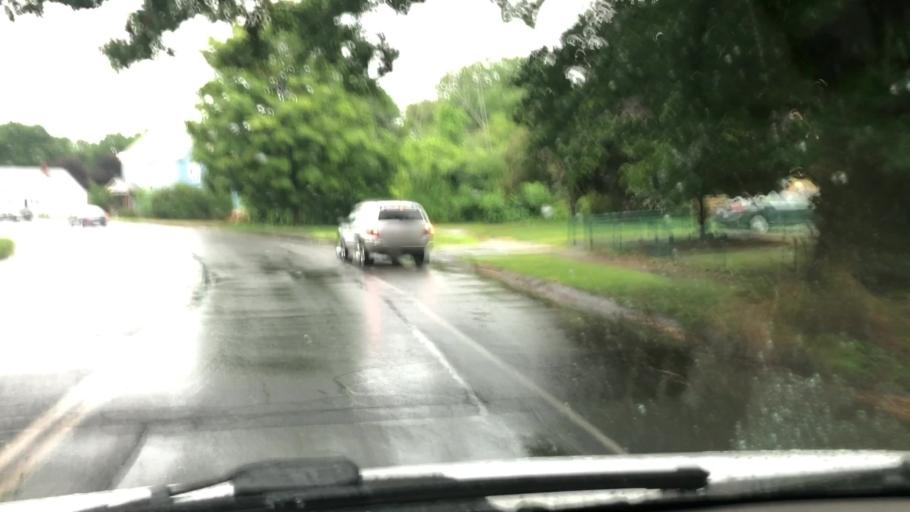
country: US
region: Massachusetts
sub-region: Berkshire County
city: Pittsfield
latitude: 42.4478
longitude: -73.2335
